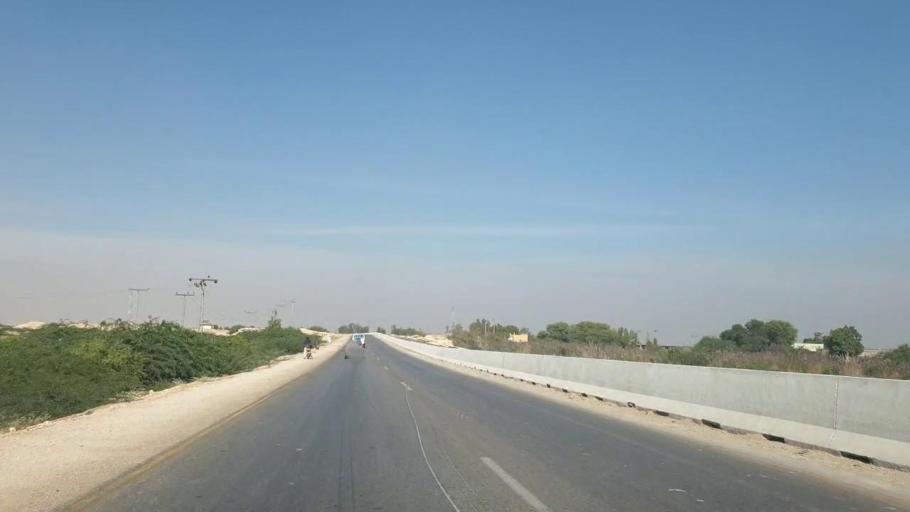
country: PK
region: Sindh
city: Hala
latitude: 25.7091
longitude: 68.2958
